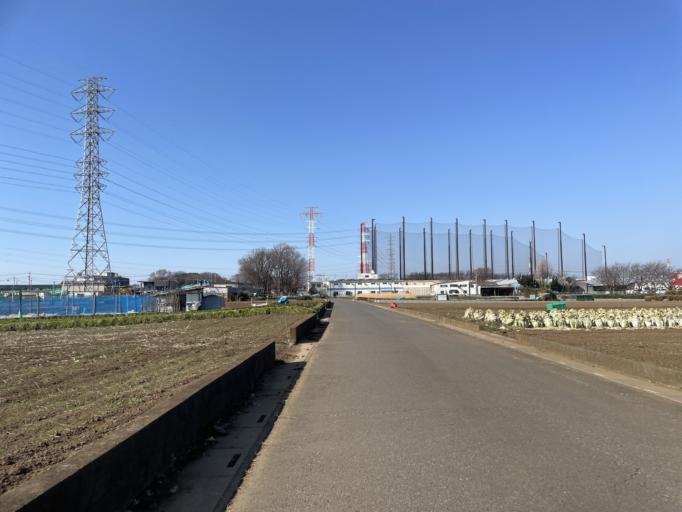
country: JP
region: Saitama
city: Oi
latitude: 35.8218
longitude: 139.5361
